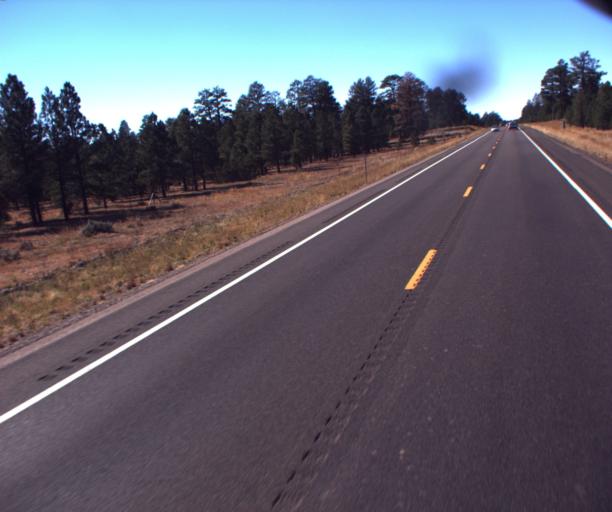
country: US
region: Arizona
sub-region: Apache County
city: Saint Michaels
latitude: 35.6975
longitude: -109.2793
